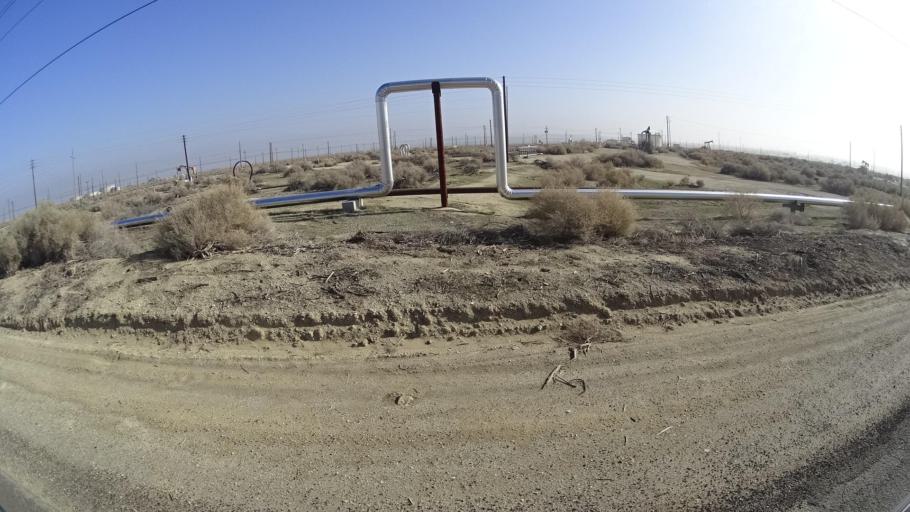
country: US
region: California
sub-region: Kern County
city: Taft Heights
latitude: 35.2178
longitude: -119.5697
